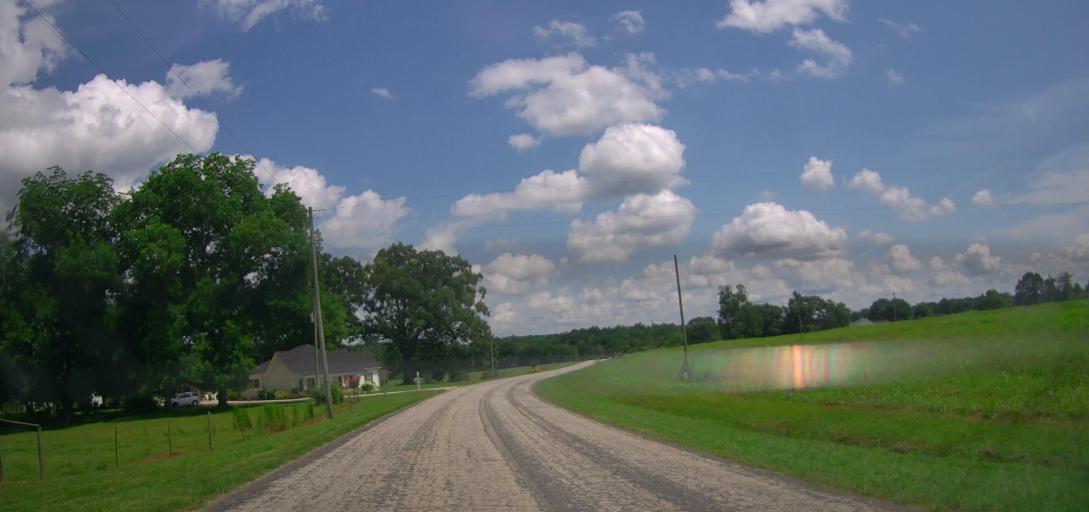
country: US
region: Georgia
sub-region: Carroll County
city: Bowdon
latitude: 33.5132
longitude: -85.3413
